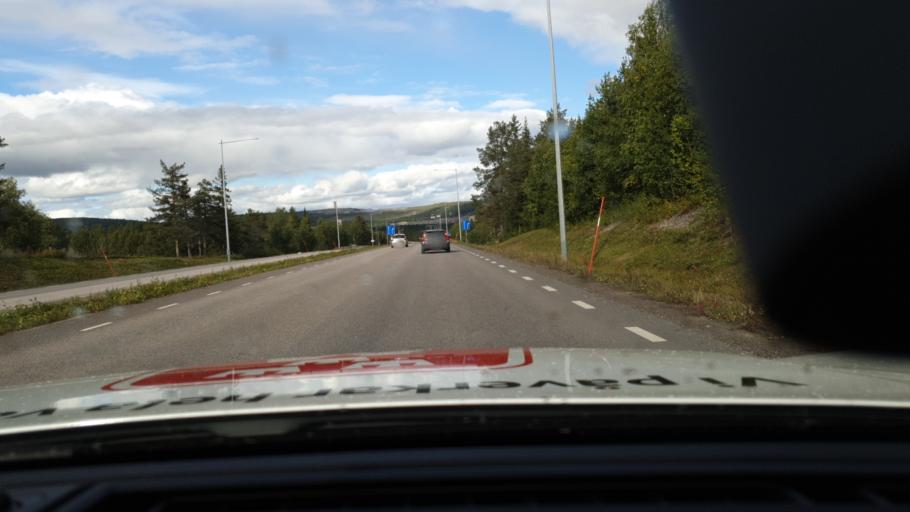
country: SE
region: Norrbotten
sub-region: Gallivare Kommun
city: Gaellivare
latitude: 67.1418
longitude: 20.6628
